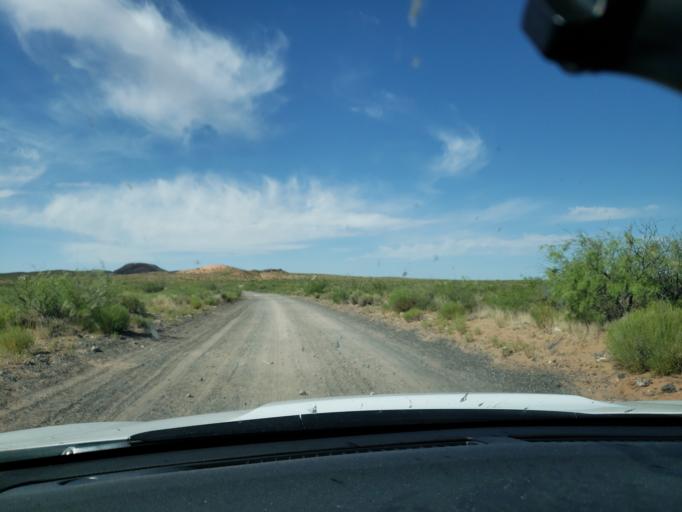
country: US
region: New Mexico
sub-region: Dona Ana County
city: San Miguel
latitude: 32.0869
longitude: -106.7874
